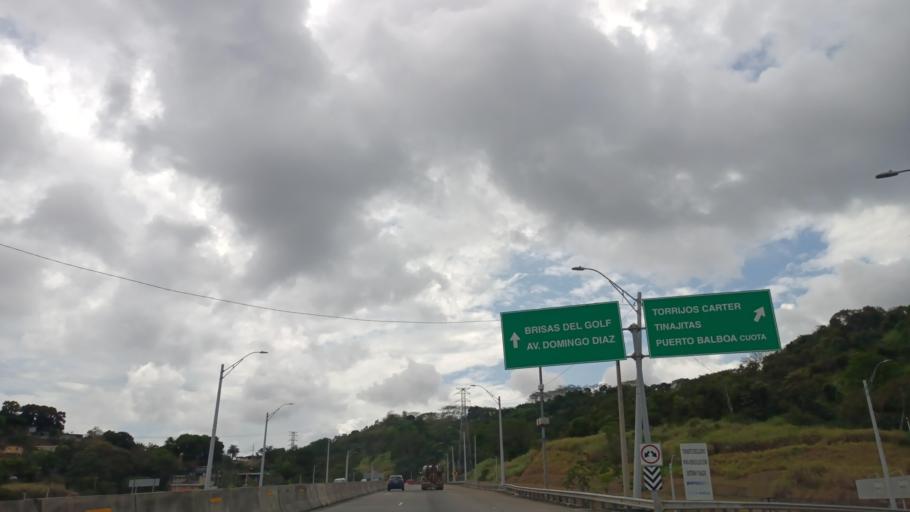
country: PA
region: Panama
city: San Miguelito
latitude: 9.0826
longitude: -79.4610
